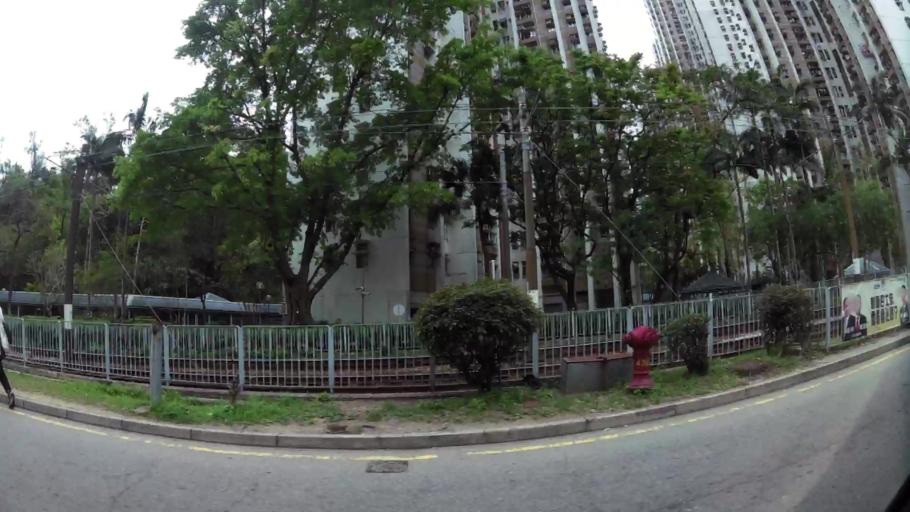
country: HK
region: Tuen Mun
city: Tuen Mun
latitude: 22.4055
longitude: 113.9637
